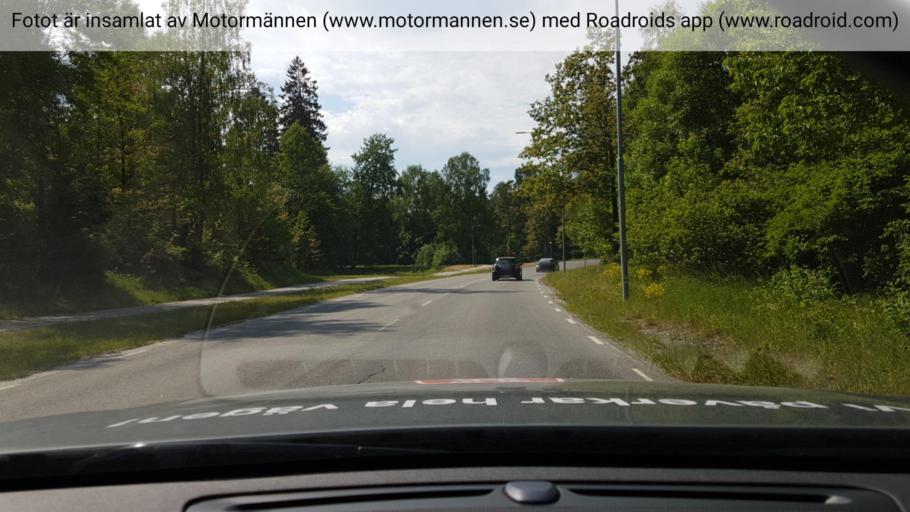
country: SE
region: Stockholm
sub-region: Lidingo
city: Brevik
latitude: 59.3490
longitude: 18.1719
